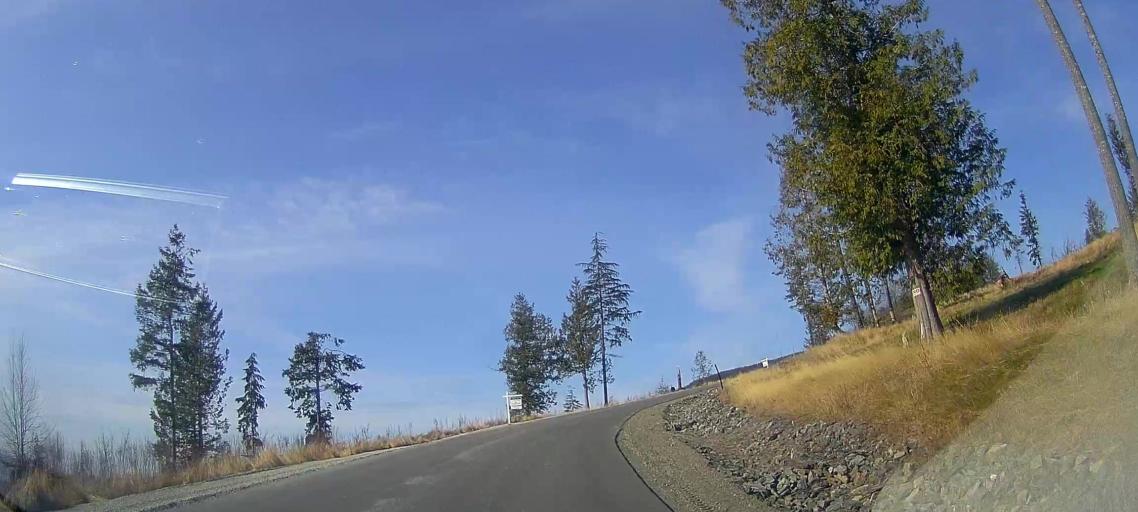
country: US
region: Washington
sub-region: Whatcom County
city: Sudden Valley
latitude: 48.5980
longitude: -122.3872
